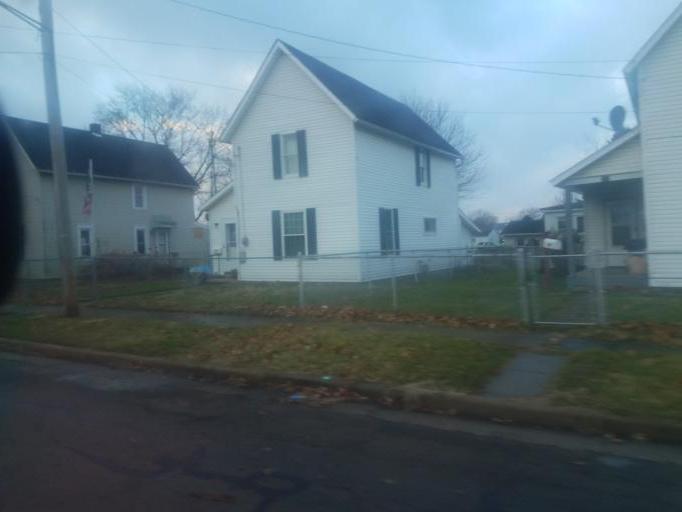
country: US
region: Ohio
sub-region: Marion County
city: Marion
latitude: 40.5973
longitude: -83.1479
